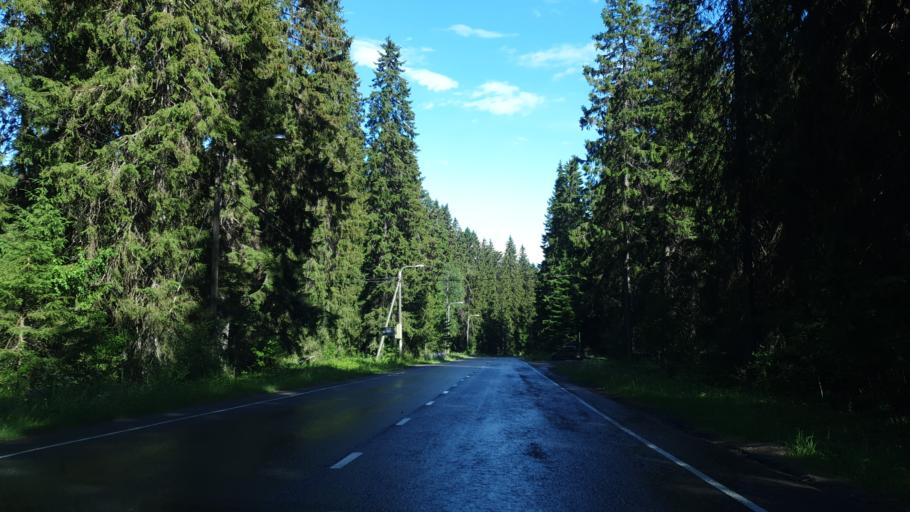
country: FI
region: Northern Savo
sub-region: Kuopio
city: Kuopio
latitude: 62.9087
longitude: 27.6636
